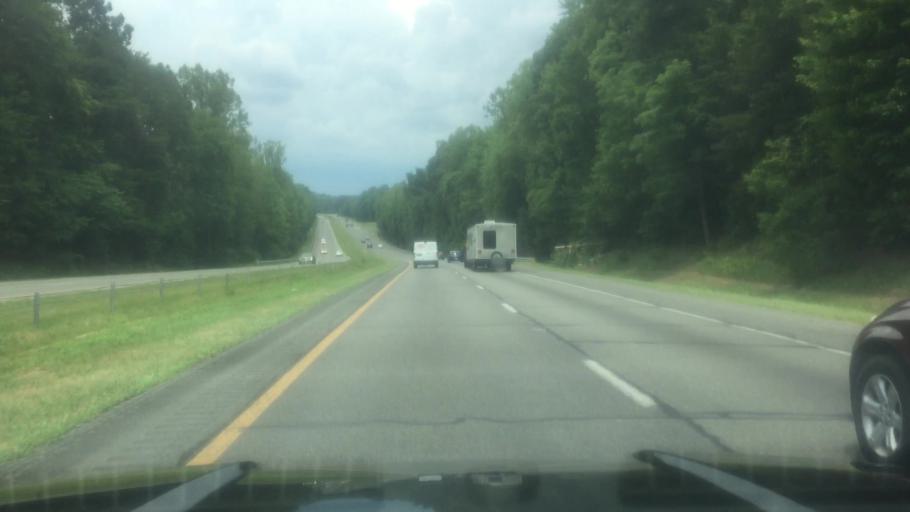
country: US
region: North Carolina
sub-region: Surry County
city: Pilot Mountain
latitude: 36.3327
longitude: -80.4533
